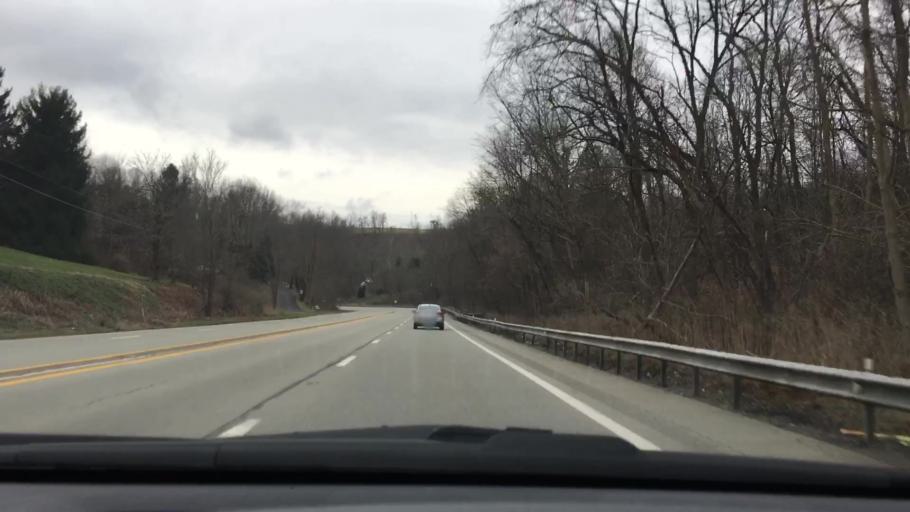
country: US
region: Pennsylvania
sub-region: Fayette County
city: Perryopolis
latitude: 40.0162
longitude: -79.7659
